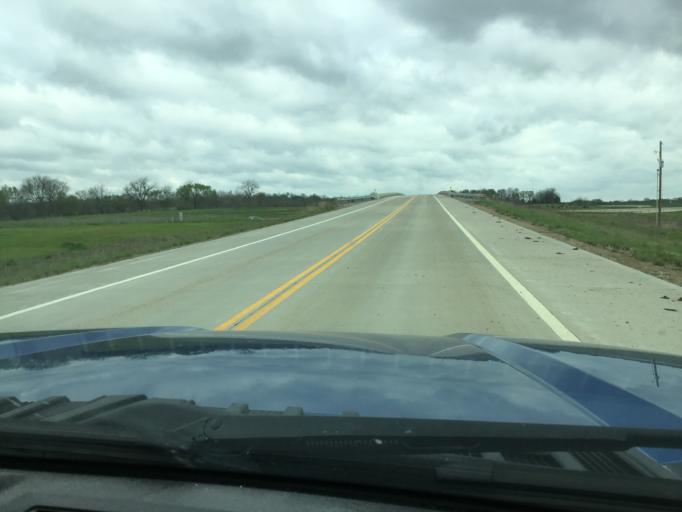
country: US
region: Kansas
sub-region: Douglas County
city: Lawrence
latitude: 38.9297
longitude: -95.1768
